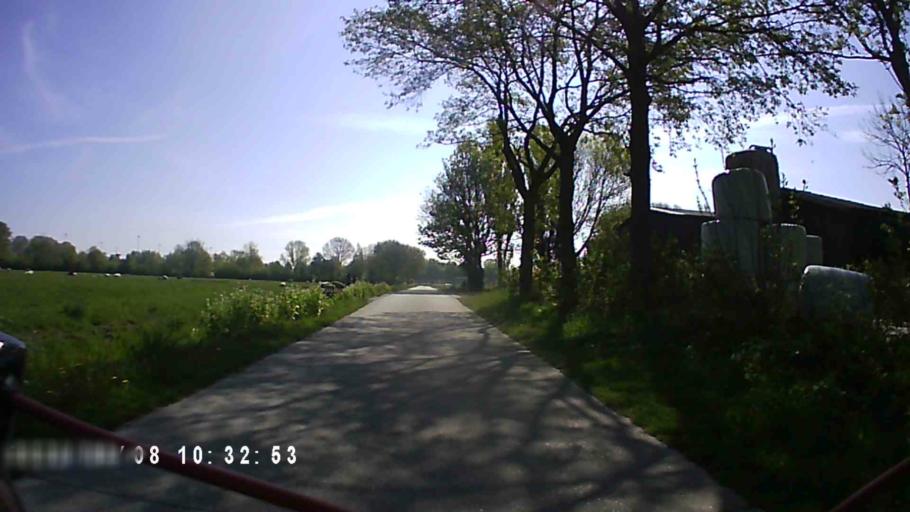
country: NL
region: Groningen
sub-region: Gemeente Winsum
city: Winsum
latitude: 53.3284
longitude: 6.5049
